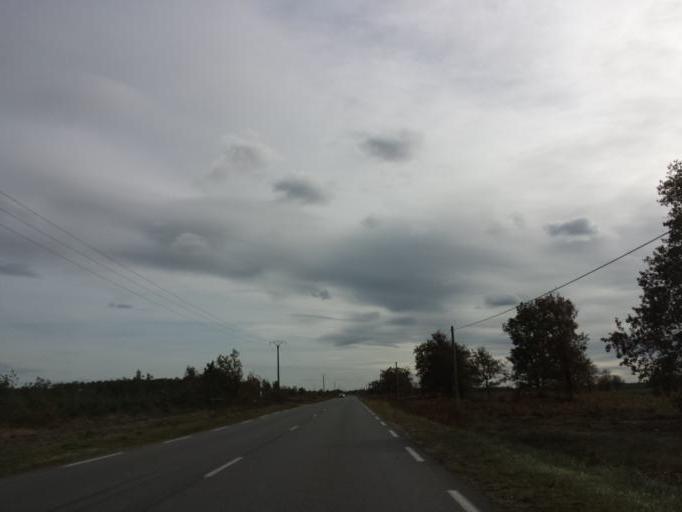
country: FR
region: Aquitaine
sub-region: Departement de la Gironde
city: Marcheprime
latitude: 44.7649
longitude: -0.9231
